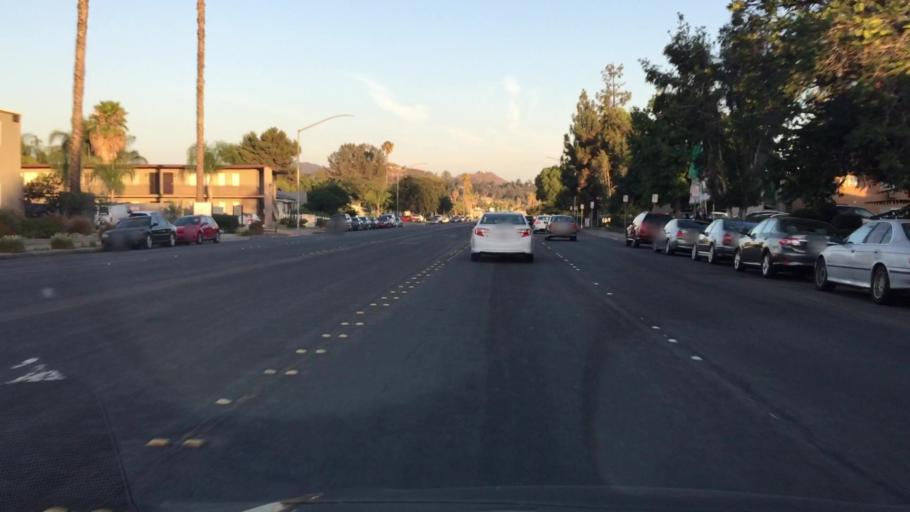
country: US
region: California
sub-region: San Diego County
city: Bostonia
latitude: 32.7916
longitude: -116.9326
